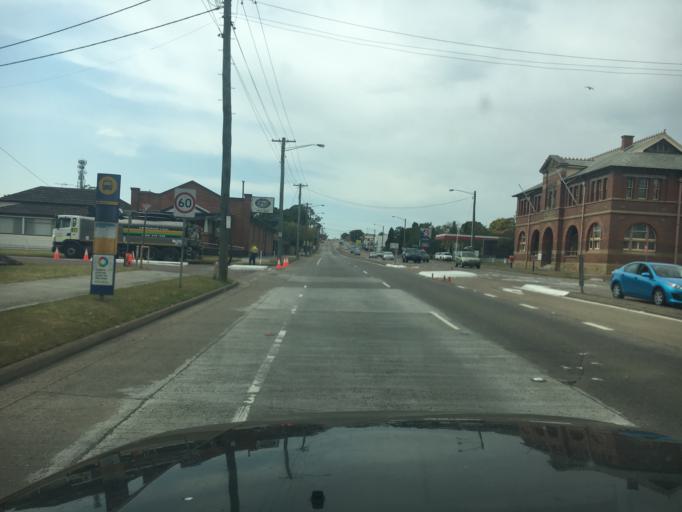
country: AU
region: New South Wales
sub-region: Maitland Municipality
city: East Maitland
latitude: -32.7476
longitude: 151.5825
